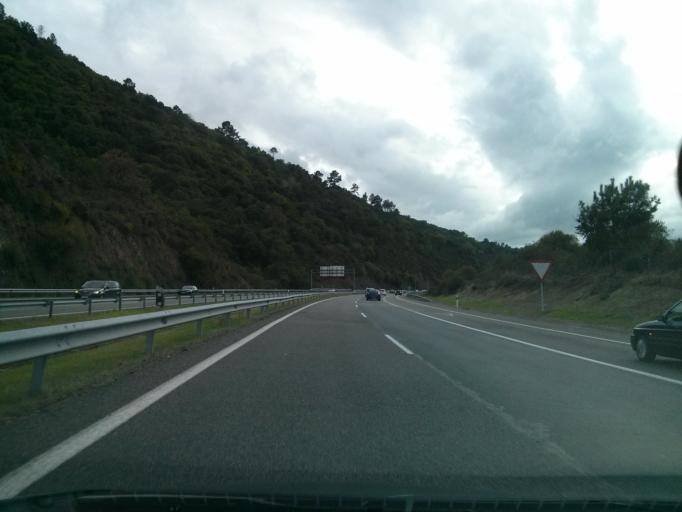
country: ES
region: Galicia
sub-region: Provincia de Ourense
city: Toen
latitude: 42.3415
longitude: -7.9283
